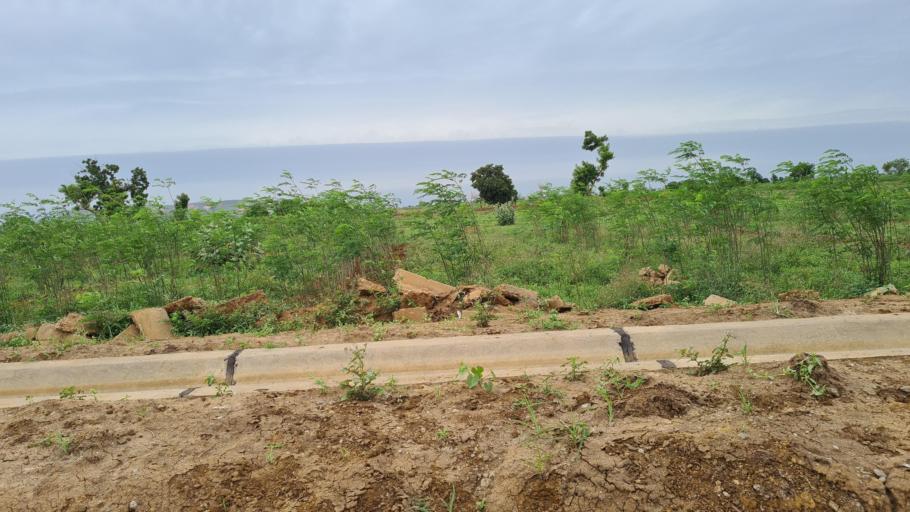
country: NE
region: Tahoua
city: Birni N Konni
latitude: 13.8300
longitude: 5.2643
